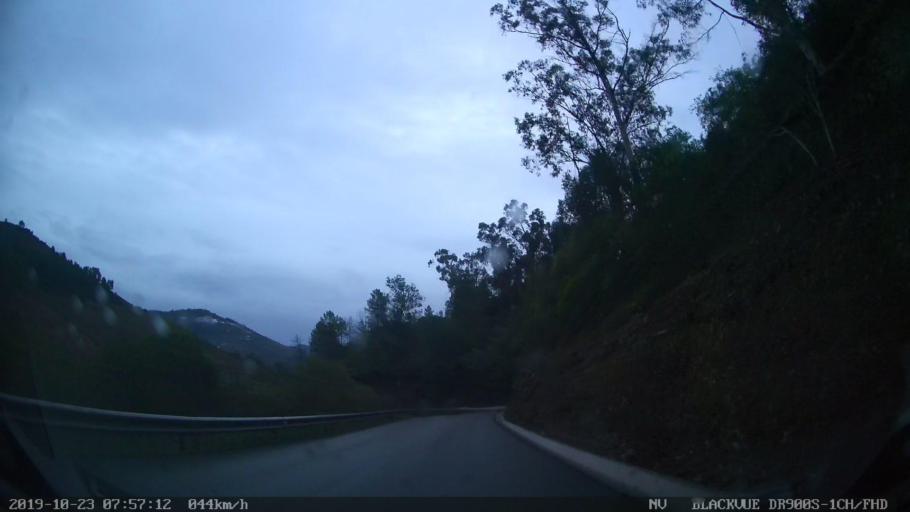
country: PT
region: Vila Real
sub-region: Sabrosa
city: Vilela
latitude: 41.2002
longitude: -7.5608
